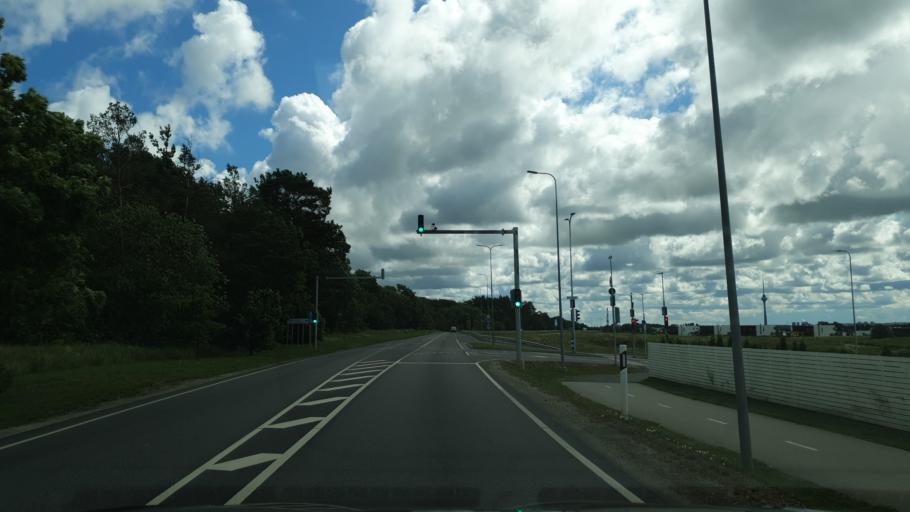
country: EE
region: Harju
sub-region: Viimsi vald
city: Viimsi
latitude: 59.5054
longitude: 24.8639
